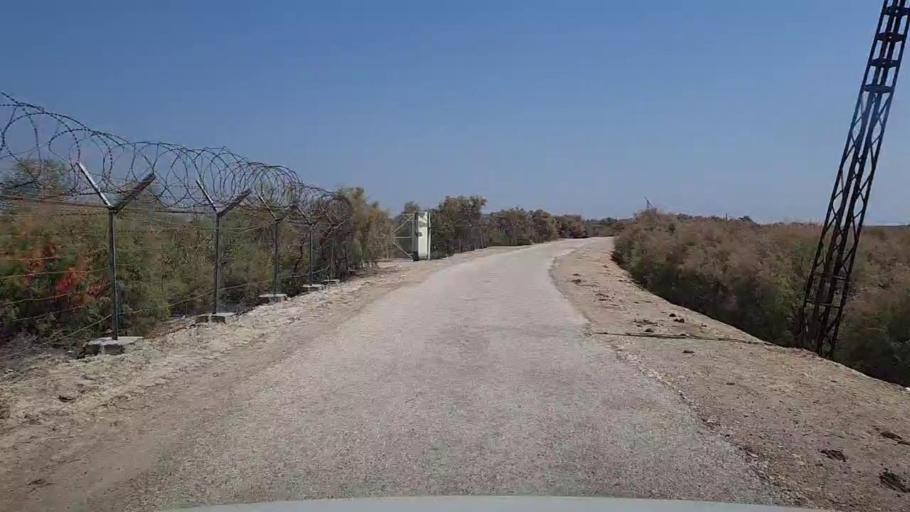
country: PK
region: Sindh
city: Kandhkot
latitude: 28.3016
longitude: 69.3503
